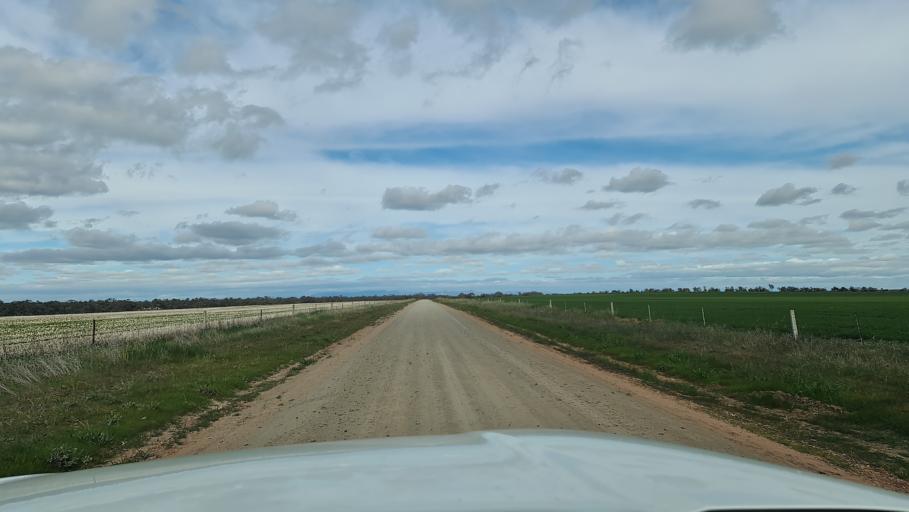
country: AU
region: Victoria
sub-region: Horsham
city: Horsham
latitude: -36.6211
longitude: 142.4116
